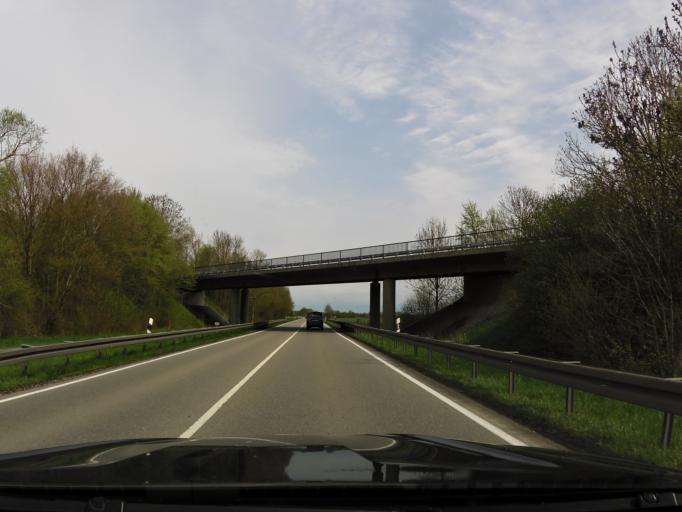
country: DE
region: Bavaria
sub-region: Upper Bavaria
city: Oberding
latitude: 48.3587
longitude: 11.8526
